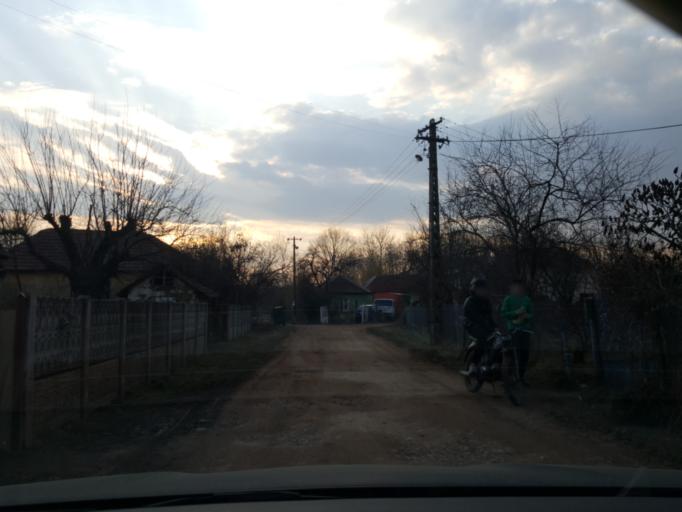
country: RS
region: Central Serbia
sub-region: Nisavski Okrug
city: Aleksinac
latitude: 43.5901
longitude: 21.6160
